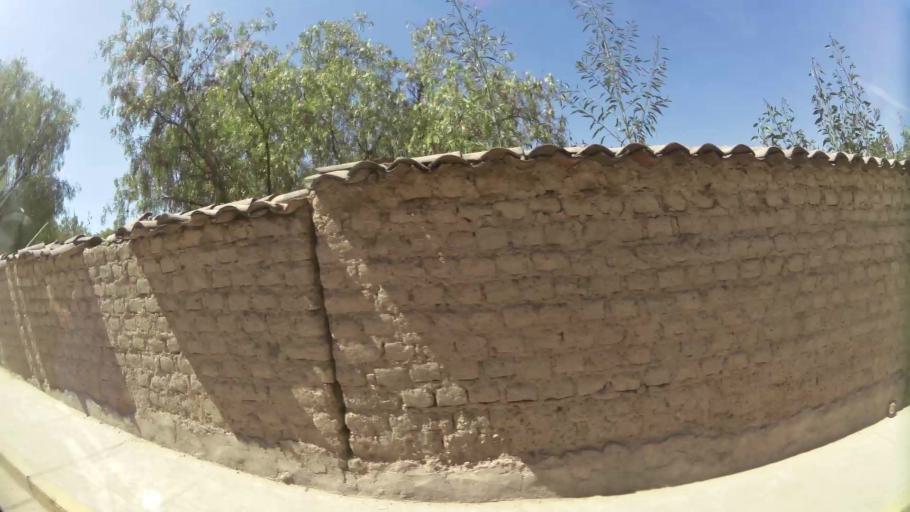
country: PE
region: Ayacucho
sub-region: Provincia de Huamanga
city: Ayacucho
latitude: -13.1683
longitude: -74.2366
